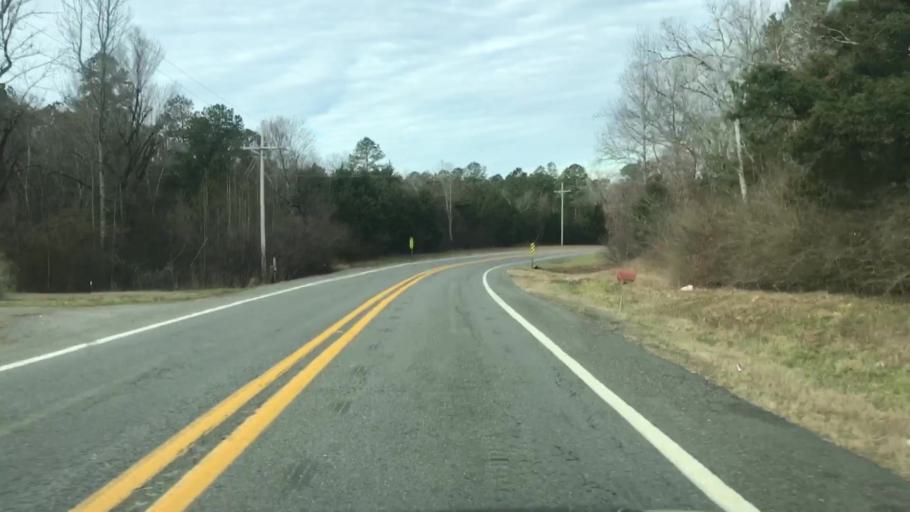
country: US
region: Arkansas
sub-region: Montgomery County
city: Mount Ida
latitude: 34.6083
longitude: -93.6824
